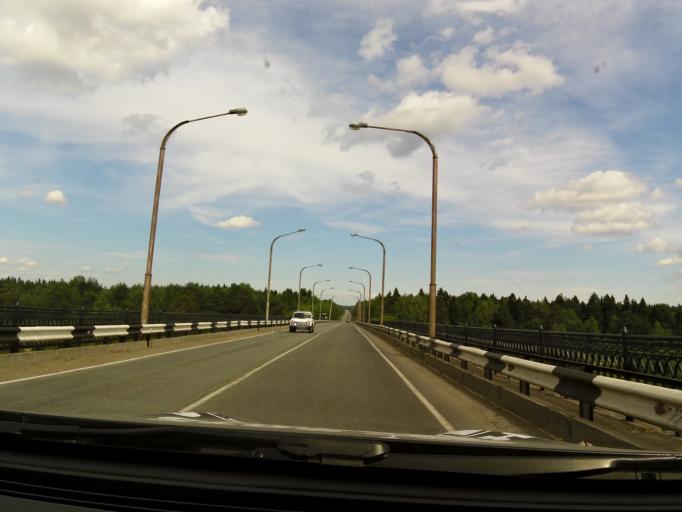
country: RU
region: Kirov
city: Slobodskoy
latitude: 58.7246
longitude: 50.1927
